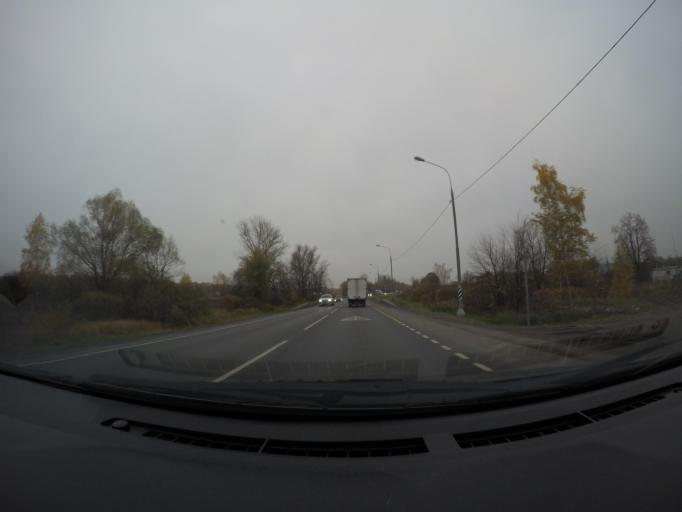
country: RU
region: Moskovskaya
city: Bronnitsy
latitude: 55.3843
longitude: 38.1898
